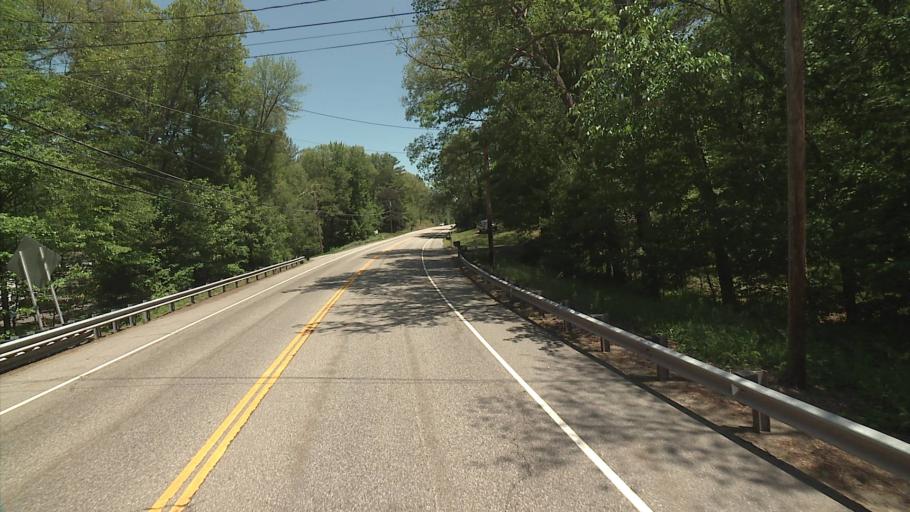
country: US
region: Connecticut
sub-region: Tolland County
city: Tolland
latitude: 41.8945
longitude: -72.3982
